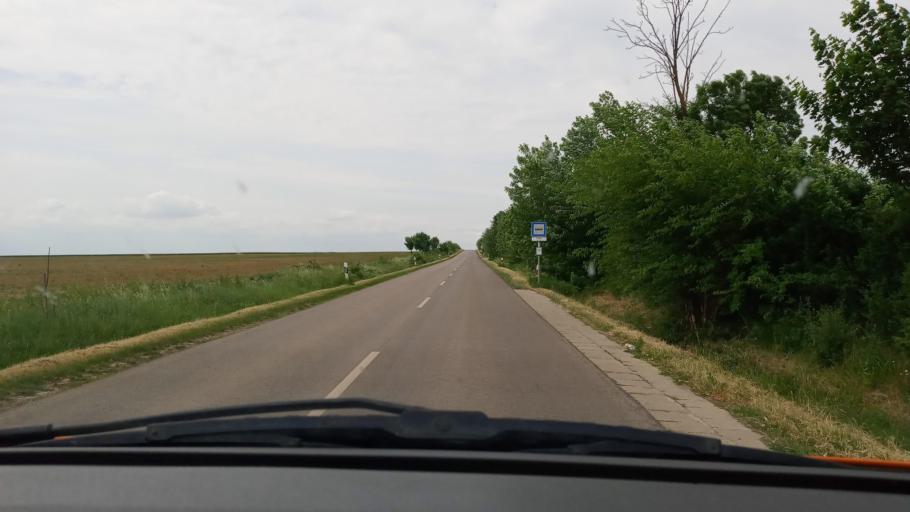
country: HU
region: Baranya
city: Vajszlo
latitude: 45.9408
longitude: 18.0746
